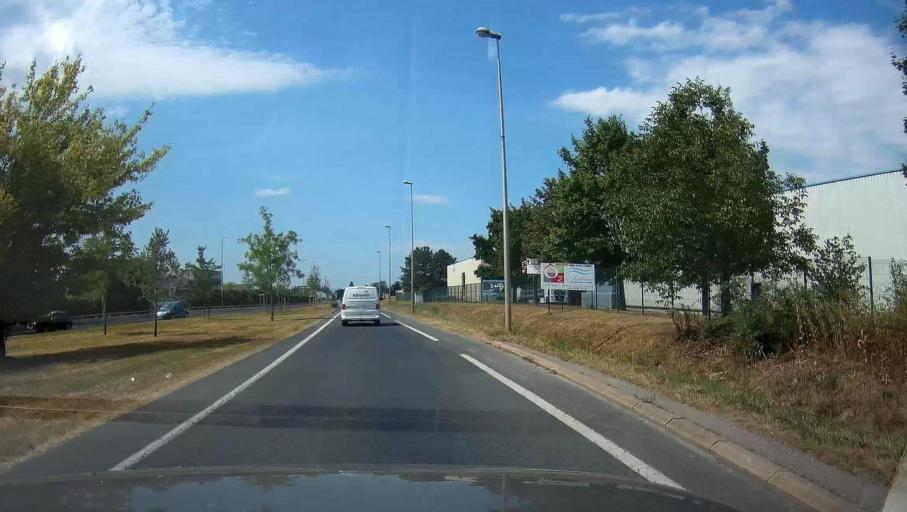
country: FR
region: Rhone-Alpes
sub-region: Departement du Rhone
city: Genay
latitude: 45.8919
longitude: 4.8251
